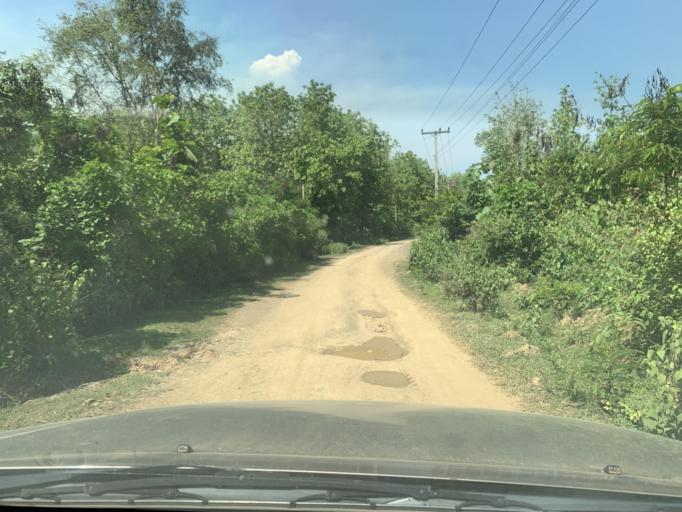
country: LA
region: Louangphabang
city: Louangphabang
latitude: 19.9249
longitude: 102.2727
